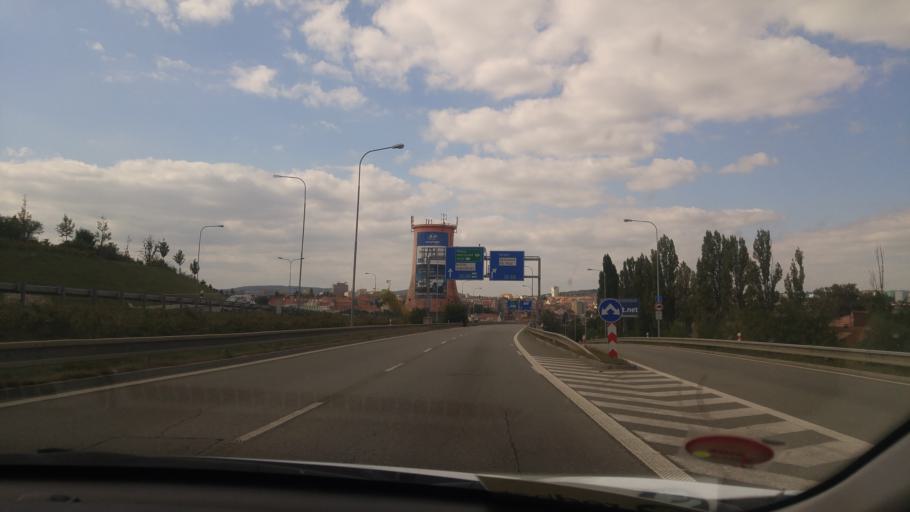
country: CZ
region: South Moravian
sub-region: Mesto Brno
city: Brno
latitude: 49.2202
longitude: 16.6099
